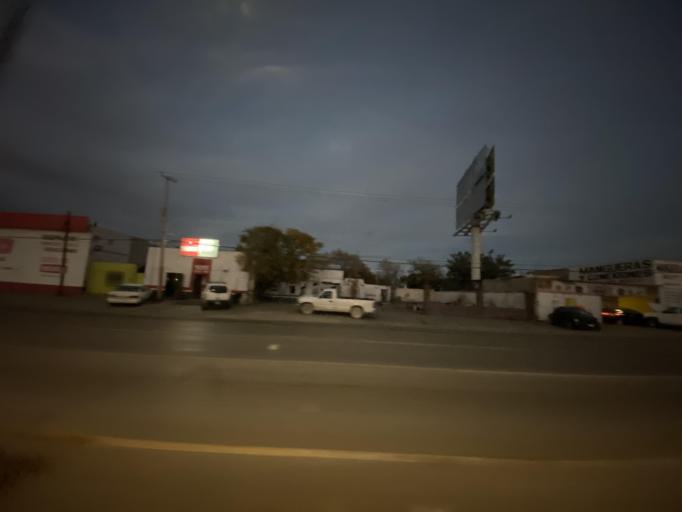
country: MX
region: Chihuahua
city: Ciudad Juarez
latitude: 31.7040
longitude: -106.4459
